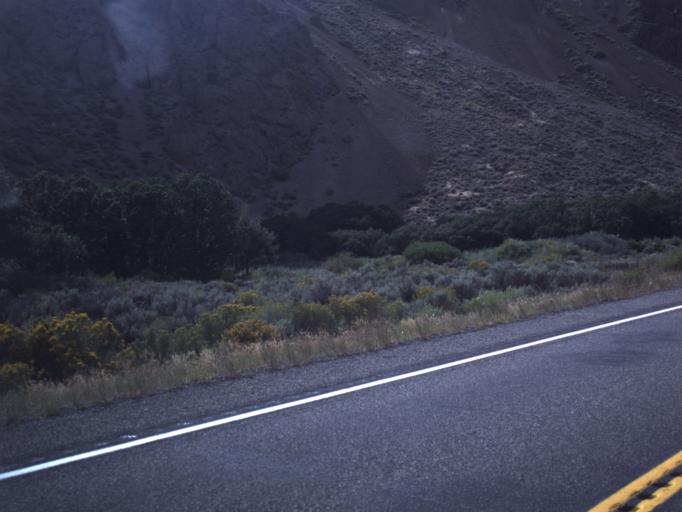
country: US
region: Utah
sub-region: Sevier County
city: Monroe
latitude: 38.4964
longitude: -112.2549
